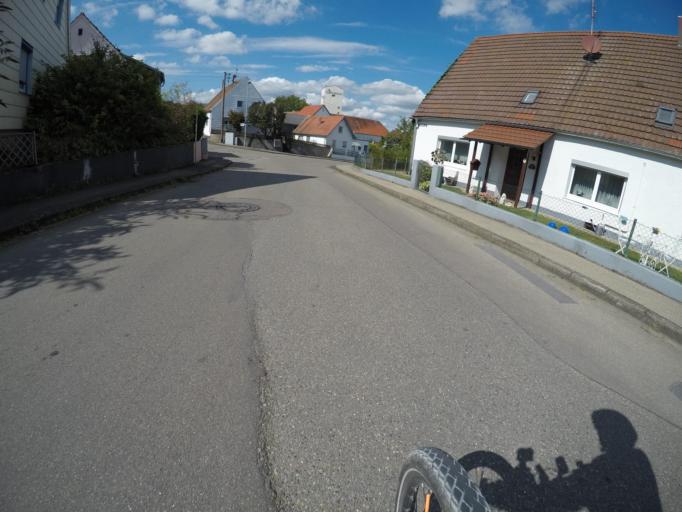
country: DE
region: Bavaria
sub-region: Swabia
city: Wittislingen
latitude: 48.6162
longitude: 10.4167
